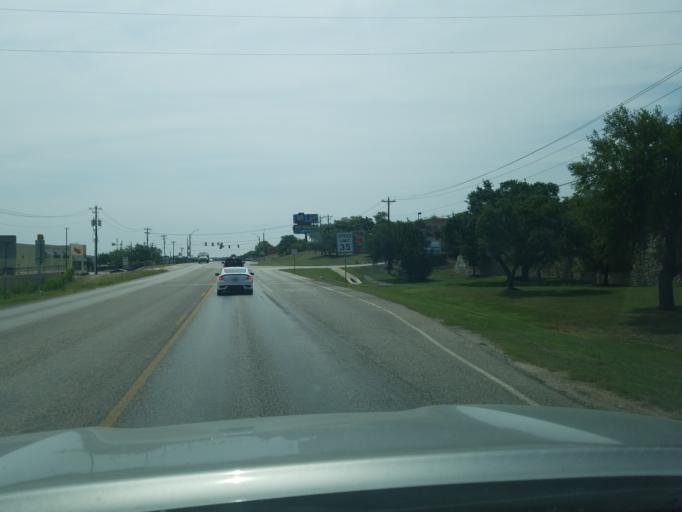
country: US
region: Texas
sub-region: Comal County
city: Bulverde
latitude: 29.7989
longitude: -98.4318
